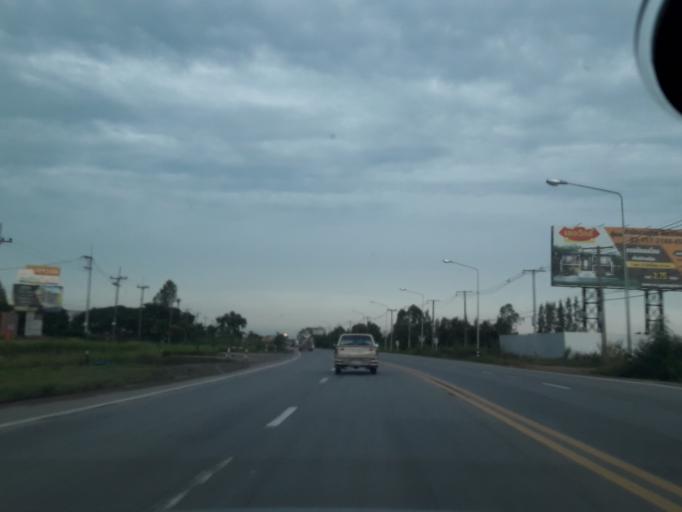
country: TH
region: Pathum Thani
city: Ban Rangsit
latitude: 14.0528
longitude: 100.7471
